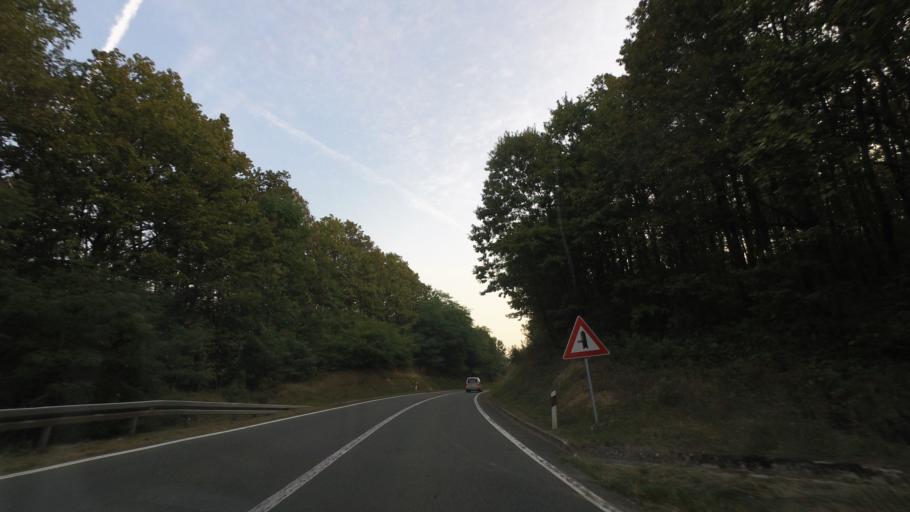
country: HR
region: Brodsko-Posavska
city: Cernik
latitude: 45.2770
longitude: 17.4023
